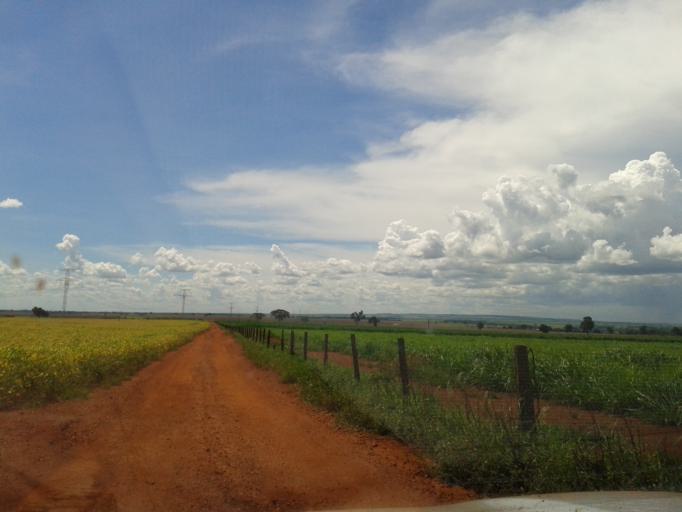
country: BR
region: Minas Gerais
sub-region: Capinopolis
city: Capinopolis
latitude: -18.7007
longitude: -49.7851
